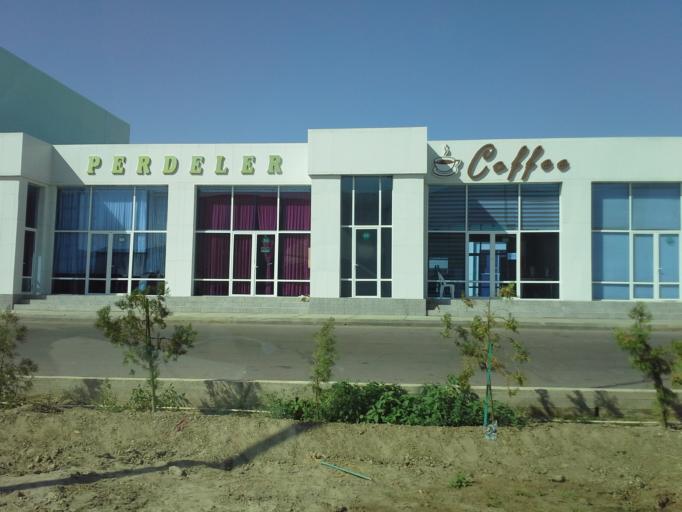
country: TM
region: Dasoguz
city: Dasoguz
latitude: 41.8083
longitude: 59.9555
